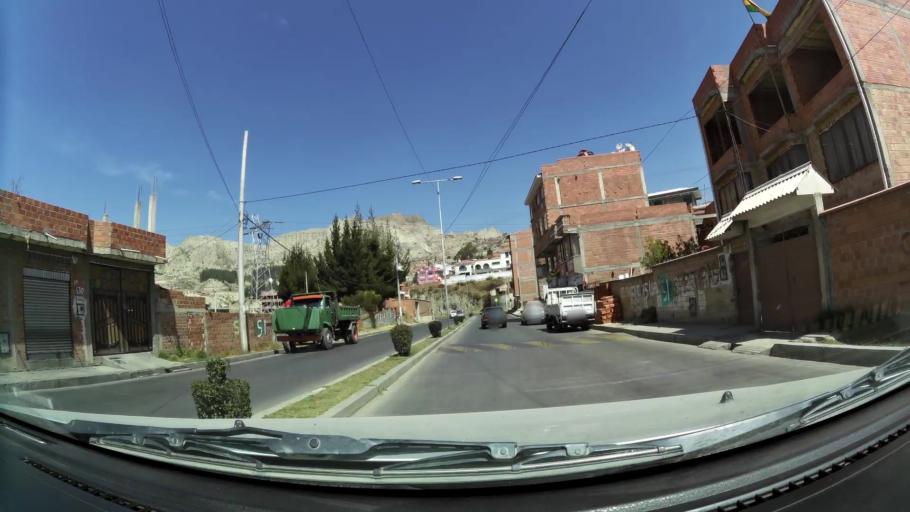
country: BO
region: La Paz
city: La Paz
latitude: -16.5308
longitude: -68.1274
